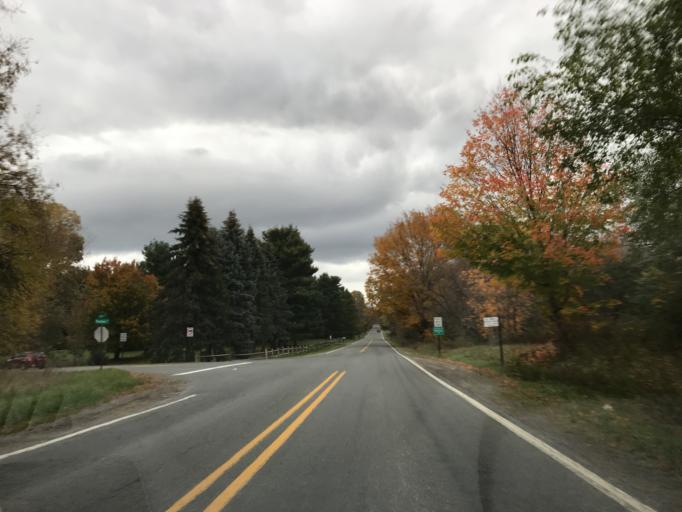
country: US
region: Michigan
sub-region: Washtenaw County
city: Ann Arbor
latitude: 42.3457
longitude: -83.7023
